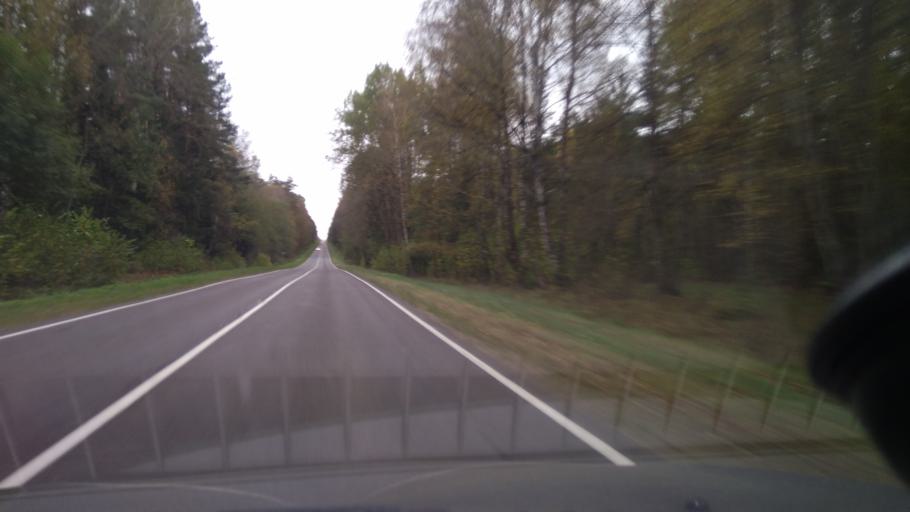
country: BY
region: Minsk
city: Druzhny
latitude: 53.6324
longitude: 27.8873
